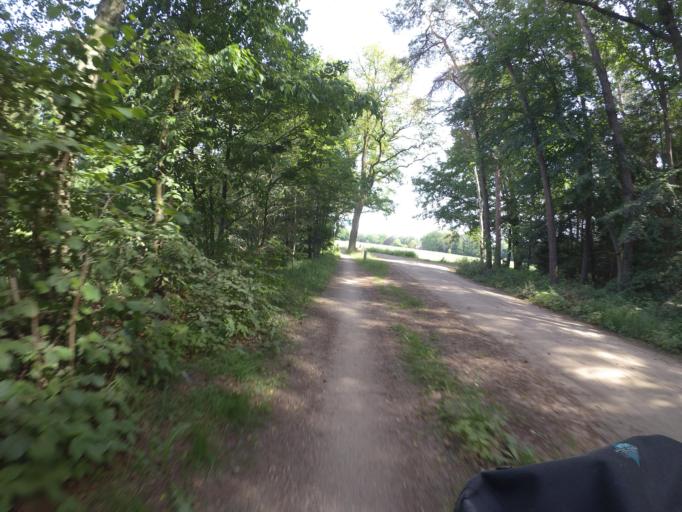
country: NL
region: Gelderland
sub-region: Gemeente Winterswijk
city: Winterswijk
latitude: 51.9353
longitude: 6.6858
